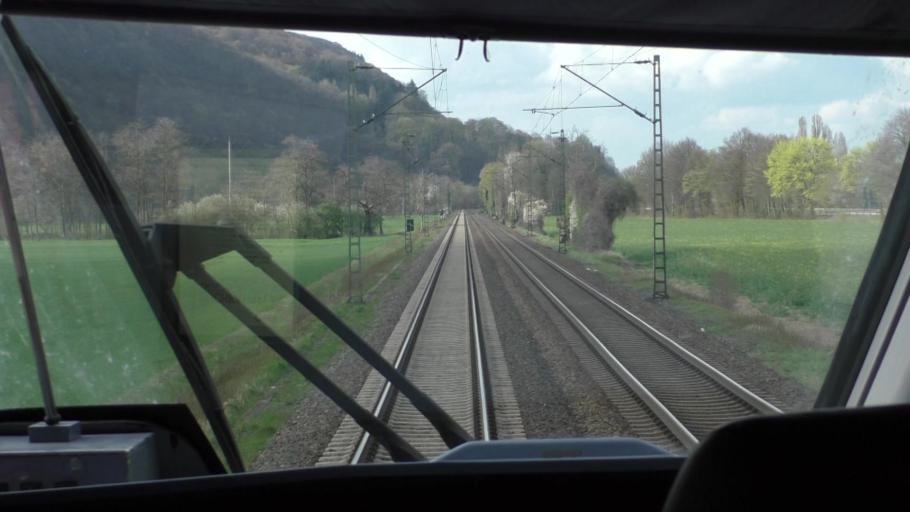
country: DE
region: Rheinland-Pfalz
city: Hammerstein
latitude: 50.4598
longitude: 7.3582
